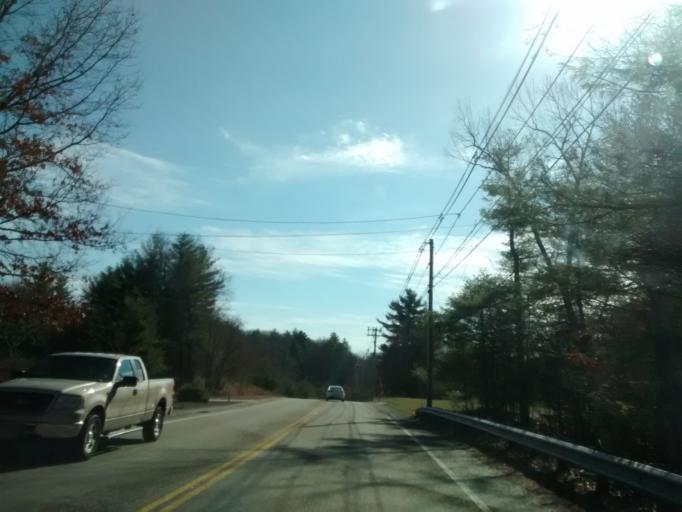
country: US
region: Massachusetts
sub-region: Worcester County
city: Uxbridge
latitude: 42.1014
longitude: -71.6047
